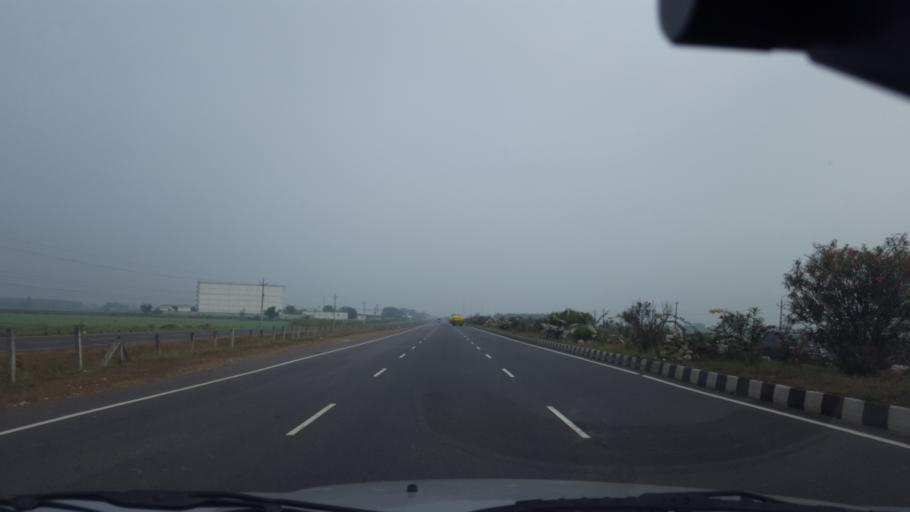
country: IN
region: Andhra Pradesh
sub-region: Guntur
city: Chilakalurupet
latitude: 16.0359
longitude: 80.1331
